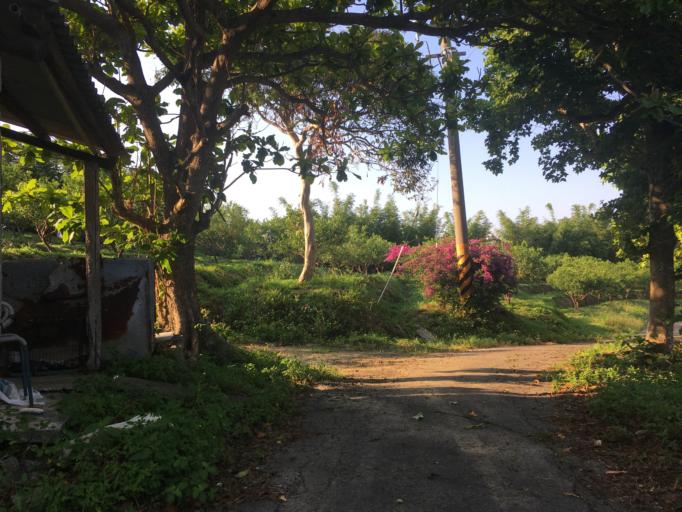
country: TW
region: Taiwan
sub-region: Hsinchu
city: Hsinchu
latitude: 24.7394
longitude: 120.9878
